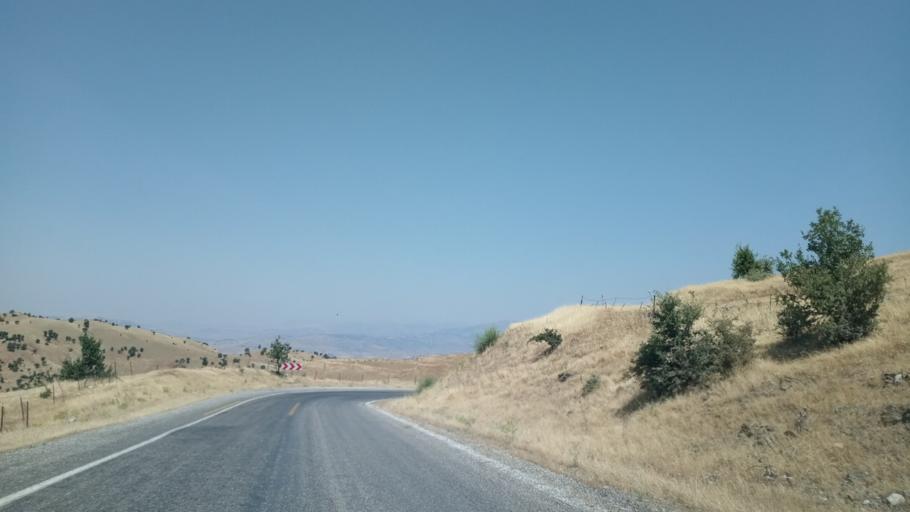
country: TR
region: Siirt
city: Dilektepe
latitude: 38.0725
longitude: 41.8280
